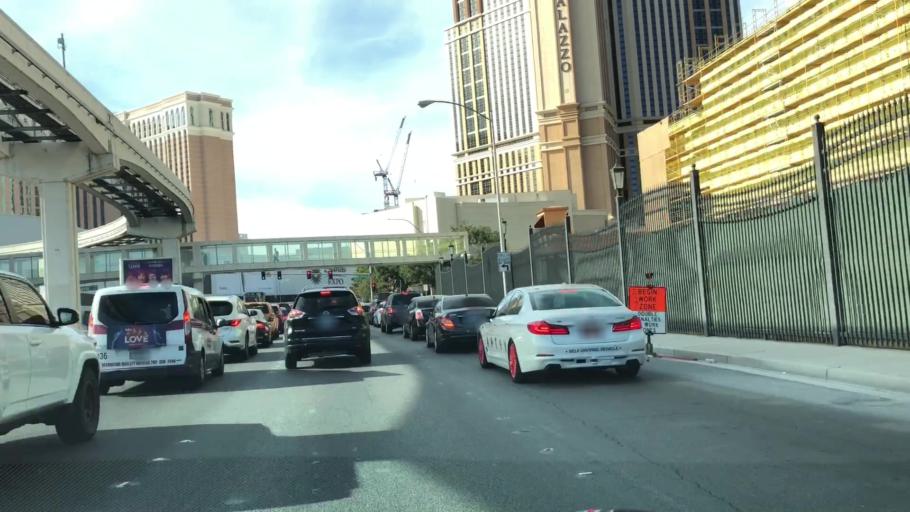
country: US
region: Nevada
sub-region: Clark County
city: Paradise
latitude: 36.1225
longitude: -115.1629
